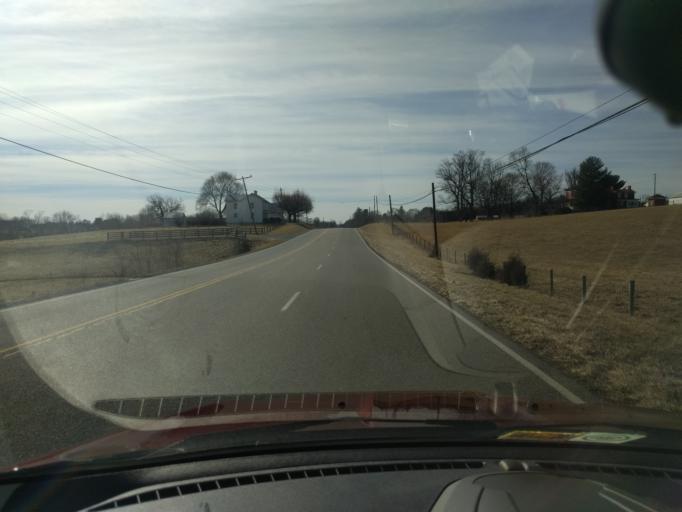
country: US
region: Virginia
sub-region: Augusta County
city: Weyers Cave
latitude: 38.2501
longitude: -78.9644
